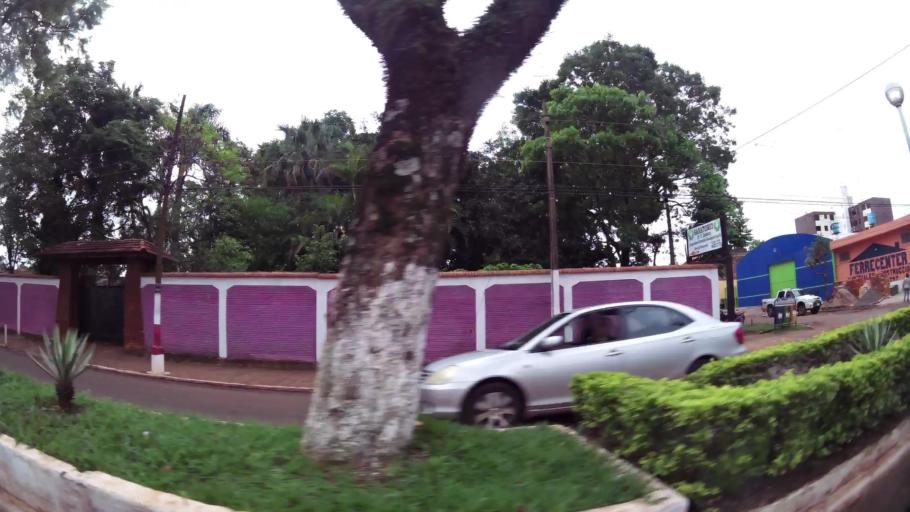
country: PY
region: Alto Parana
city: Ciudad del Este
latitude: -25.4068
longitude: -54.6347
